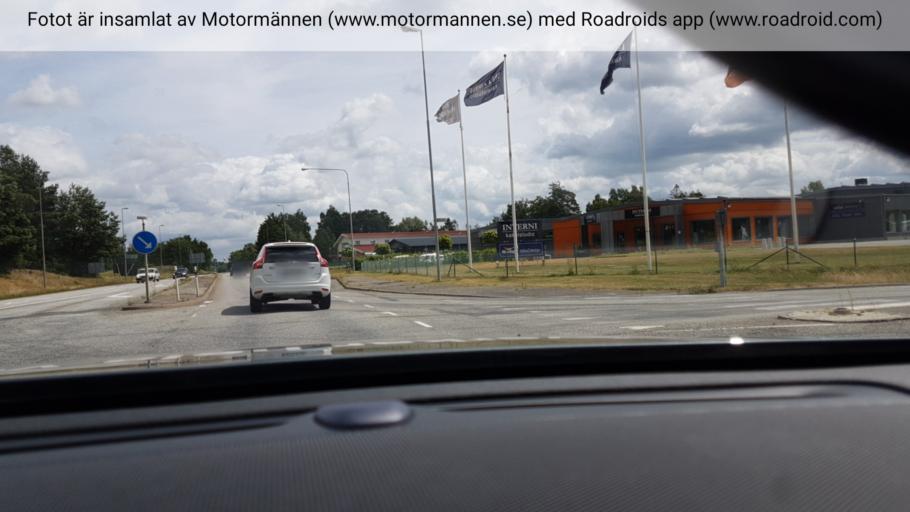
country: SE
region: Skane
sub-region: Hassleholms Kommun
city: Hassleholm
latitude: 56.1691
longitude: 13.8011
